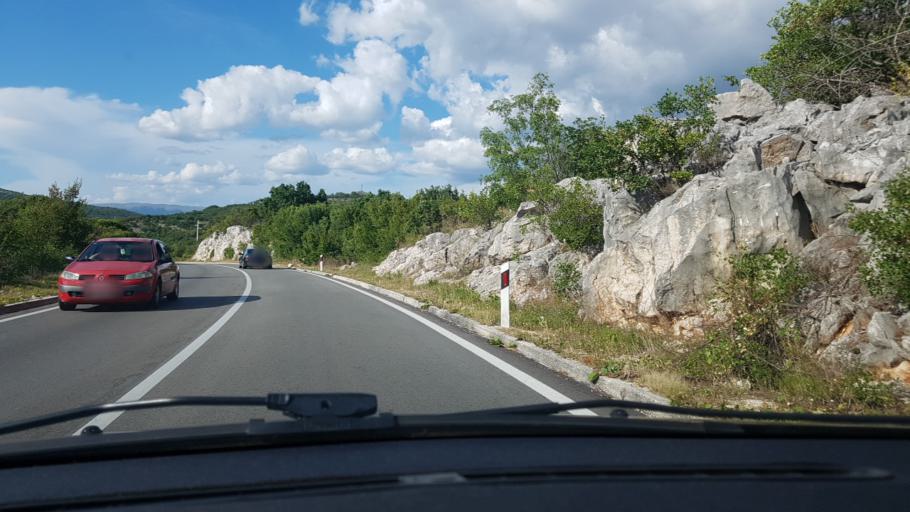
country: HR
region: Splitsko-Dalmatinska
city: Grubine
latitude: 43.4127
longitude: 17.0961
